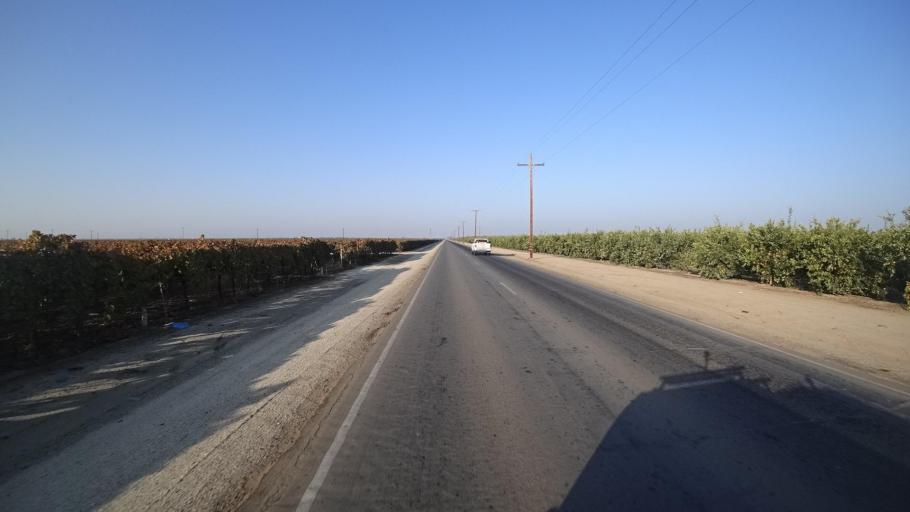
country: US
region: California
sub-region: Kern County
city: Delano
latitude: 35.7905
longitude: -119.1938
